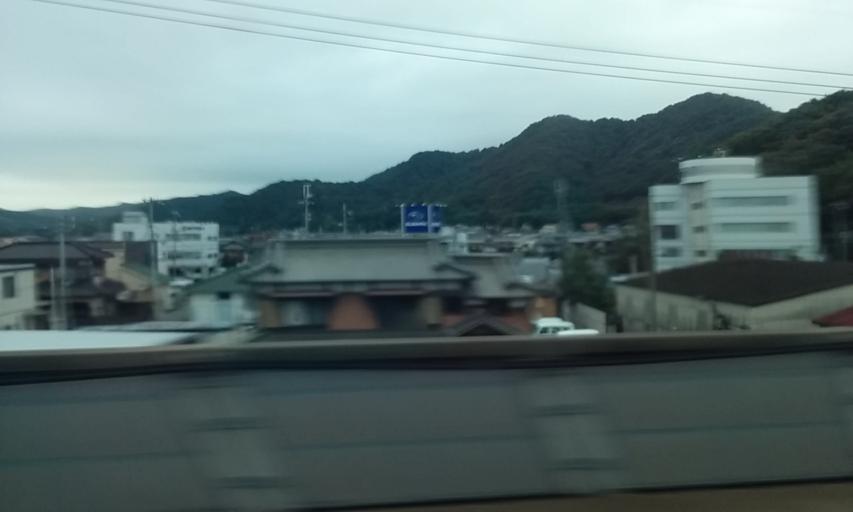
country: JP
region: Hyogo
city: Tatsunocho-tominaga
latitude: 34.8283
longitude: 134.6053
